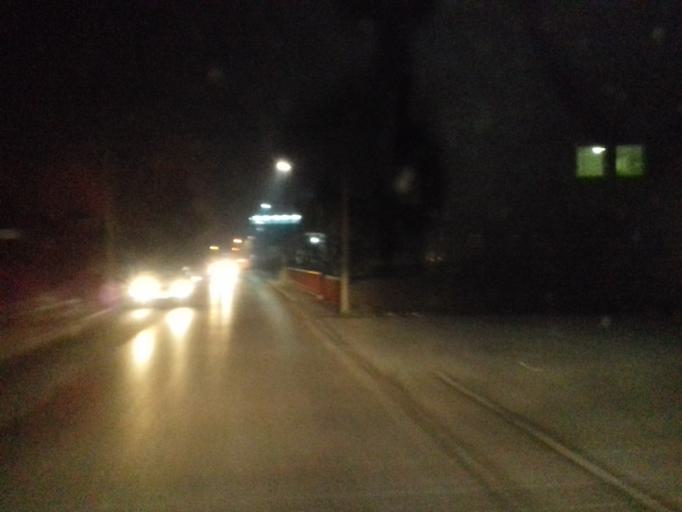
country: BA
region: Federation of Bosnia and Herzegovina
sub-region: Kanton Sarajevo
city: Sarajevo
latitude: 43.8327
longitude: 18.3150
